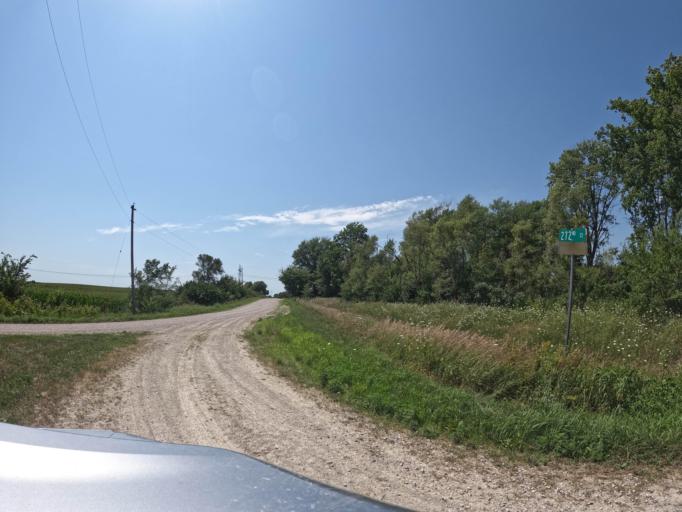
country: US
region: Iowa
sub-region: Henry County
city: Mount Pleasant
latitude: 40.9131
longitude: -91.6365
